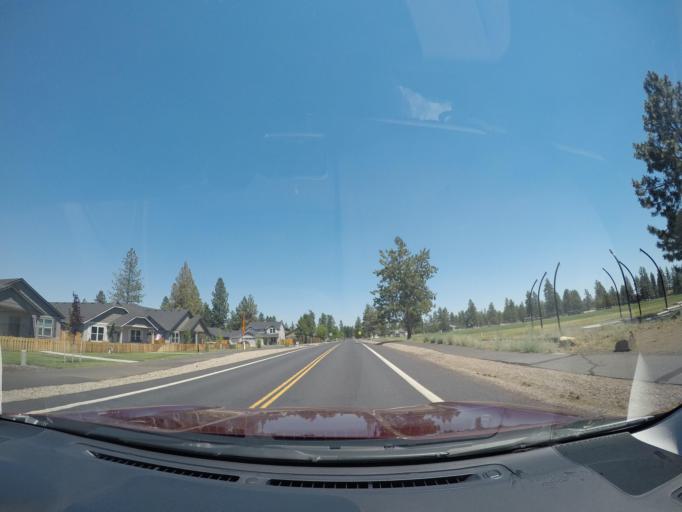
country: US
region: Oregon
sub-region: Deschutes County
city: Sisters
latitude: 44.2950
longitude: -121.5714
